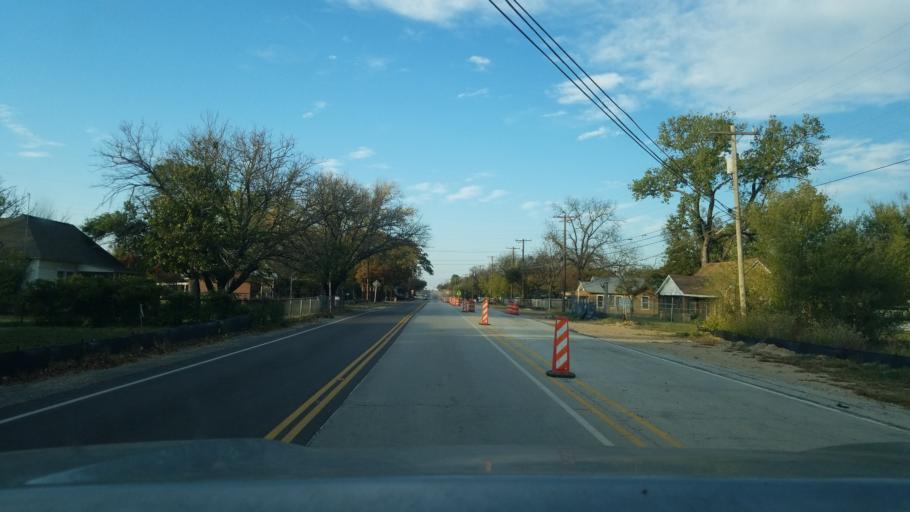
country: US
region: Texas
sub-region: Brown County
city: Lake Brownwood
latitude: 32.1011
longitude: -98.9643
